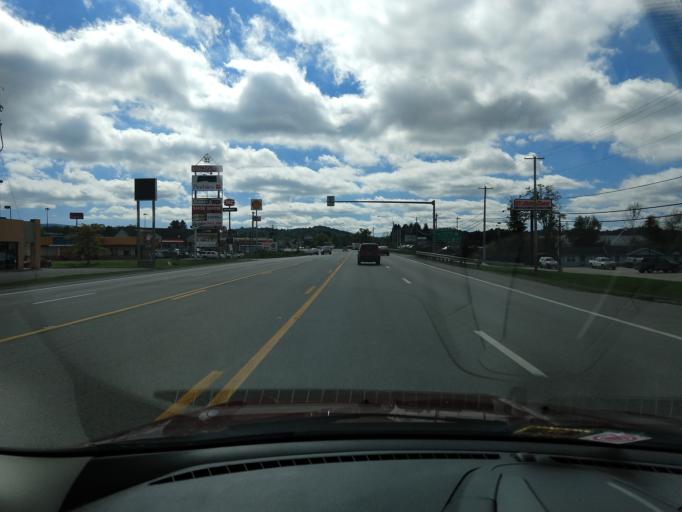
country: US
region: West Virginia
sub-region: Randolph County
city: Elkins
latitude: 38.8924
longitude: -79.8466
